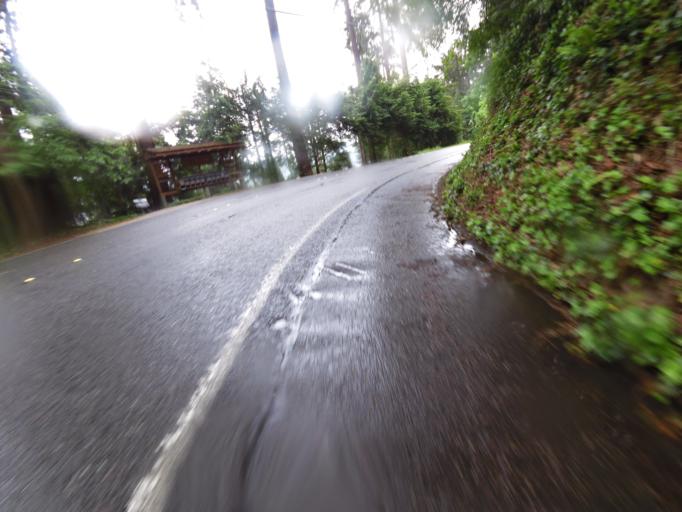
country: US
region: Washington
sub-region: King County
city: Mercer Island
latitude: 47.5538
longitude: -122.2128
